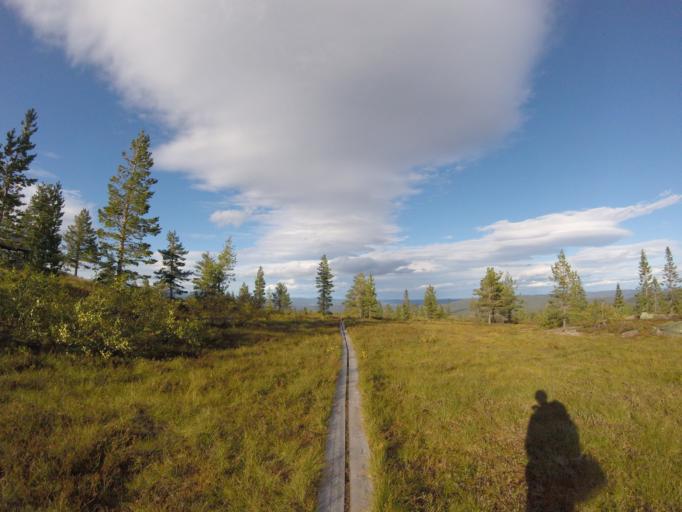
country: NO
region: Buskerud
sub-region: Flesberg
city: Lampeland
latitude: 59.7848
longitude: 9.4145
